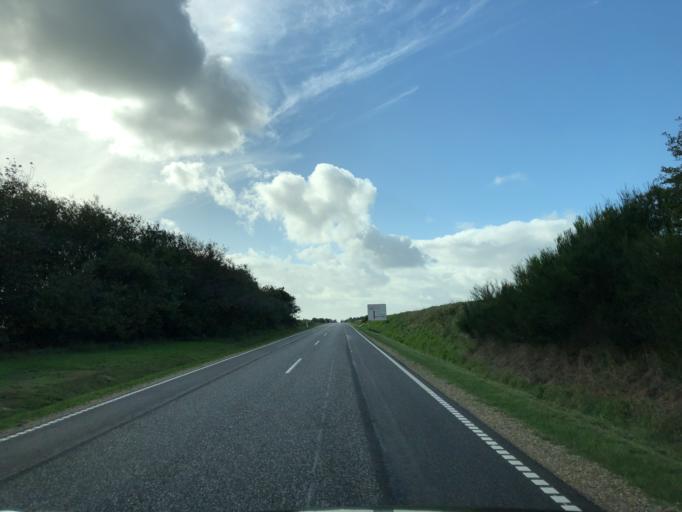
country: DK
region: Central Jutland
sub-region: Holstebro Kommune
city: Ulfborg
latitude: 56.3669
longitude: 8.4442
